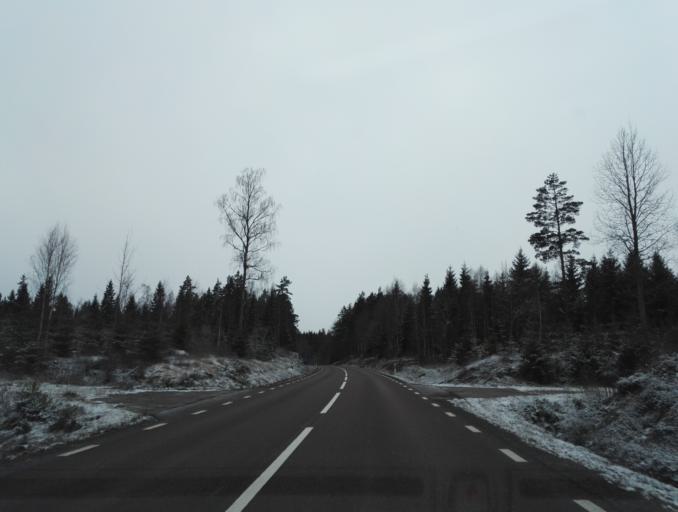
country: SE
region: Kalmar
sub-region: Hultsfreds Kommun
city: Virserum
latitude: 57.2043
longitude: 15.5175
